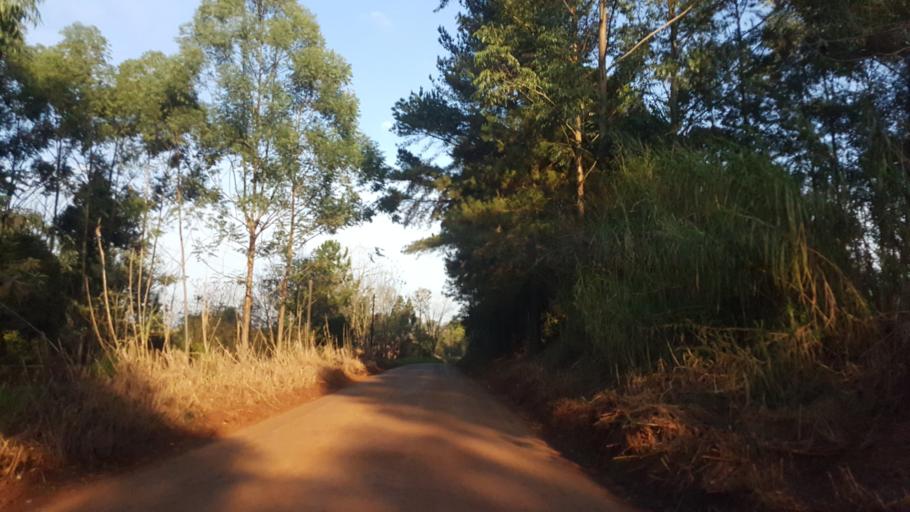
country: AR
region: Misiones
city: Capiovi
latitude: -26.8904
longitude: -55.0654
